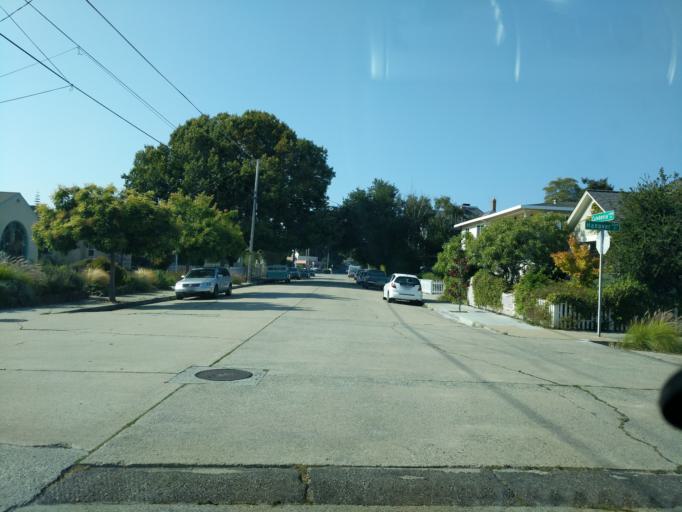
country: US
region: California
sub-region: Santa Cruz County
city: Santa Cruz
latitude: 36.9762
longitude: -122.0144
